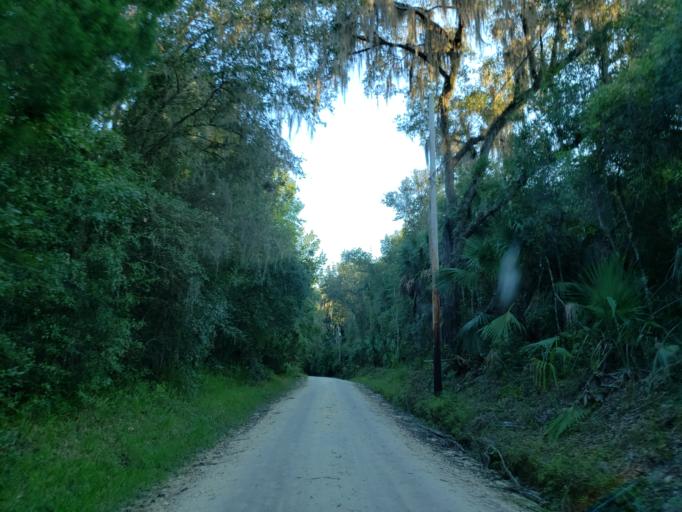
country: US
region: Florida
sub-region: Alachua County
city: Gainesville
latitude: 29.4965
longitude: -82.2828
